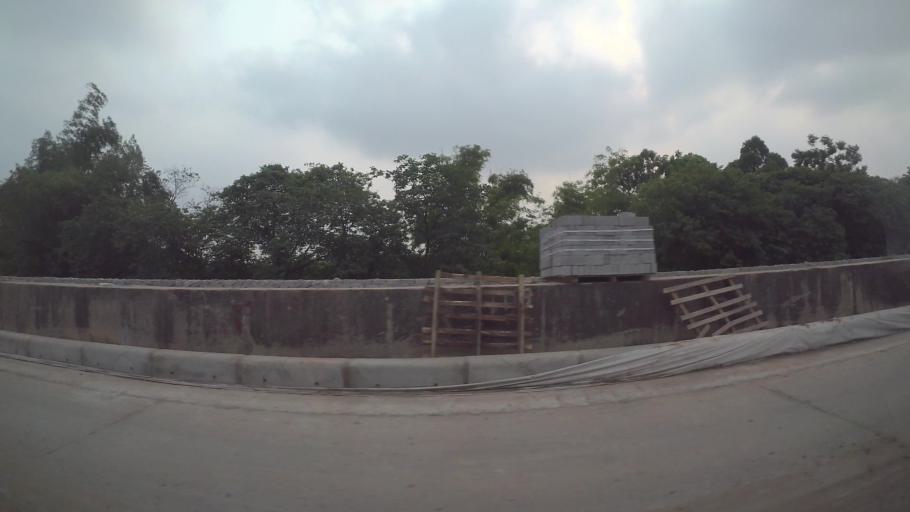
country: VN
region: Ha Noi
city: Trau Quy
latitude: 21.0207
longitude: 105.9012
